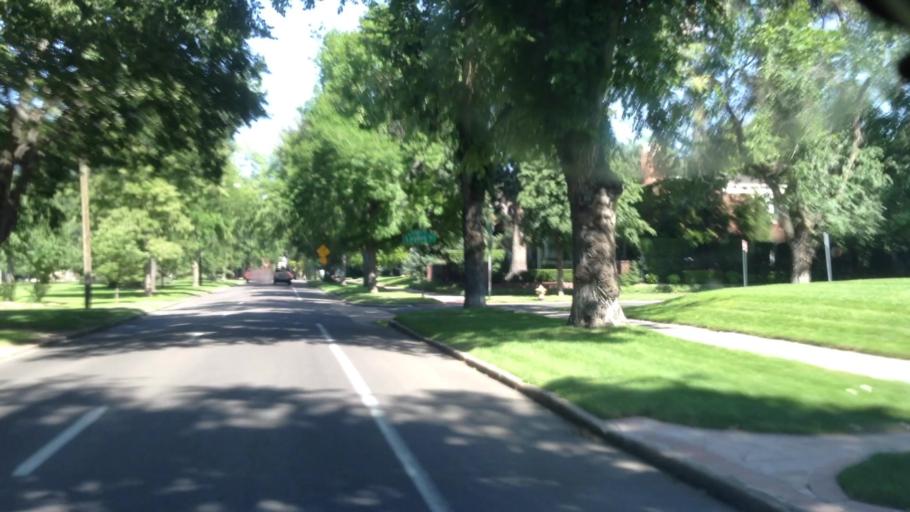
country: US
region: Colorado
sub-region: Arapahoe County
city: Glendale
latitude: 39.7434
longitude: -104.9157
